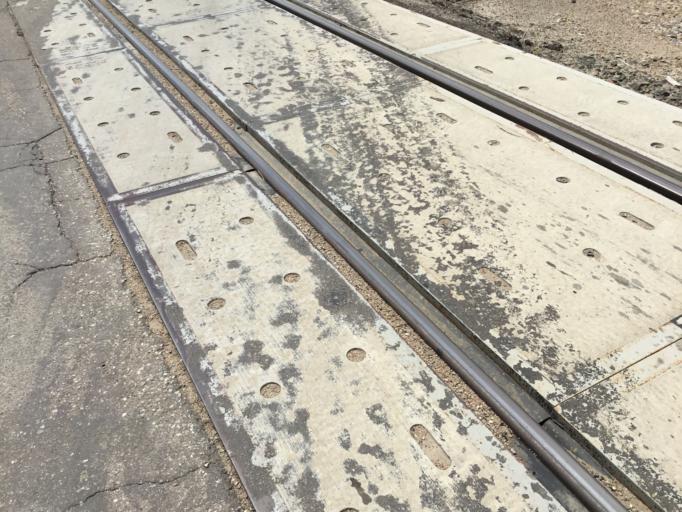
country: US
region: Kansas
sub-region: Republic County
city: Belleville
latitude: 39.7714
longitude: -97.8949
